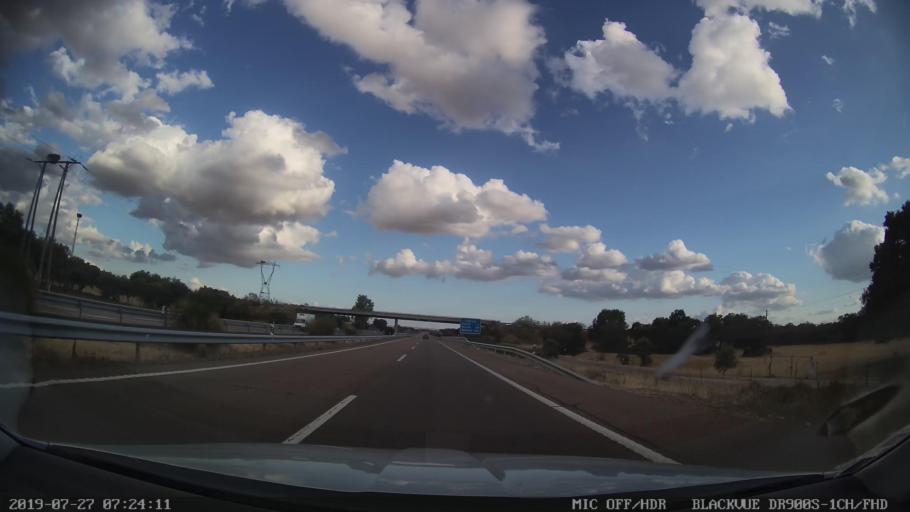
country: ES
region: Extremadura
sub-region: Provincia de Caceres
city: Puerto de Santa Cruz
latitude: 39.3032
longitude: -5.8571
